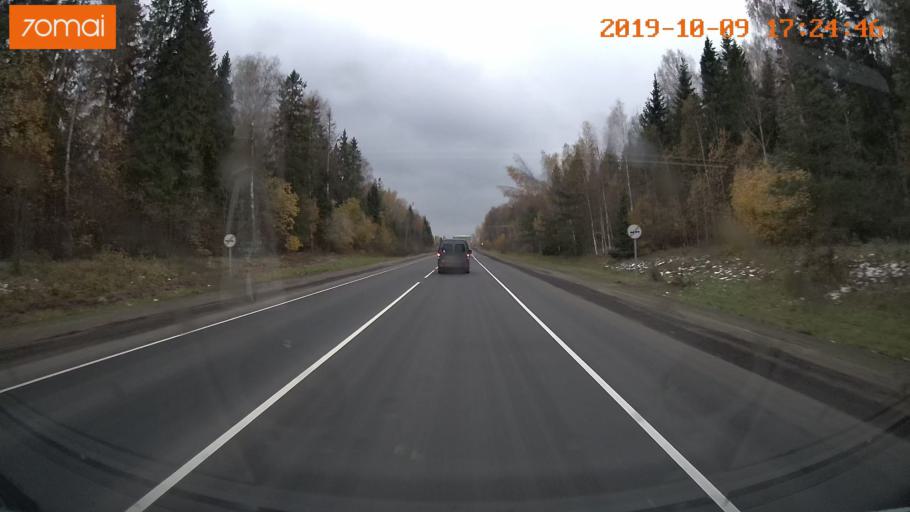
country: RU
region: Ivanovo
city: Furmanov
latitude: 57.1833
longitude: 41.1015
